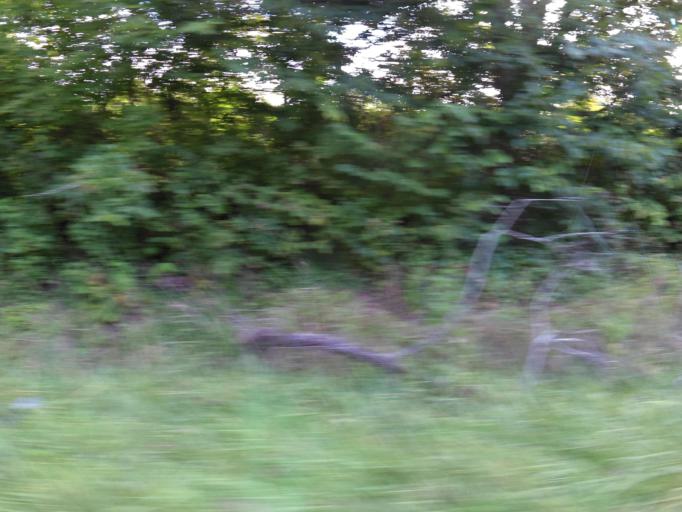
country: US
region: Kentucky
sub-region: Whitley County
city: Williamsburg
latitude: 36.7090
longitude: -84.1500
